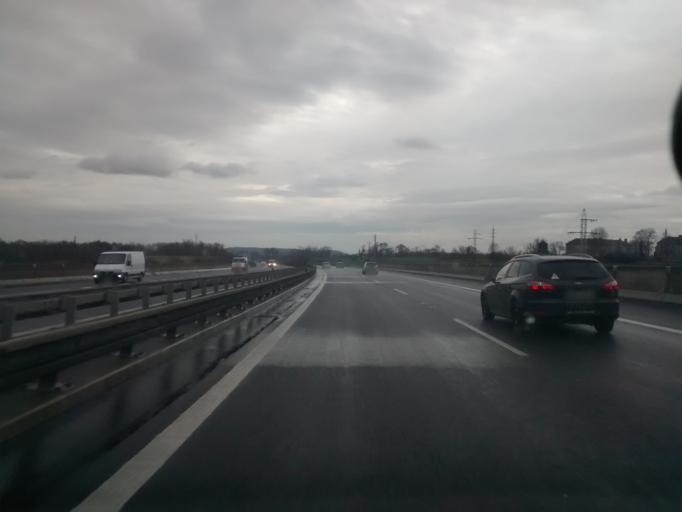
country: CZ
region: Central Bohemia
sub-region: Okres Melnik
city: Veltrusy
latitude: 50.3086
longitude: 14.3187
